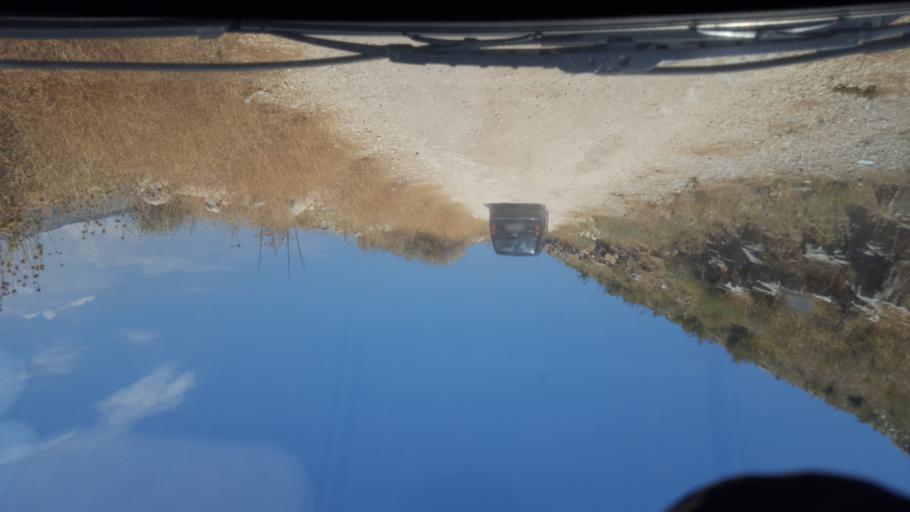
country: AL
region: Vlore
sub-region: Rrethi i Sarandes
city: Sarande
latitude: 39.8423
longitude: 20.0201
